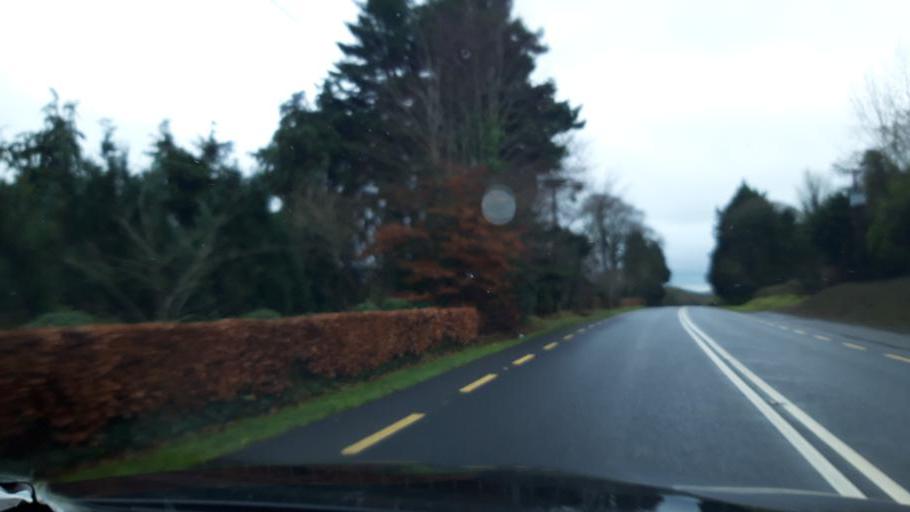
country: IE
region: Ulster
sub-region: County Monaghan
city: Castleblayney
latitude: 54.1040
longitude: -6.7112
